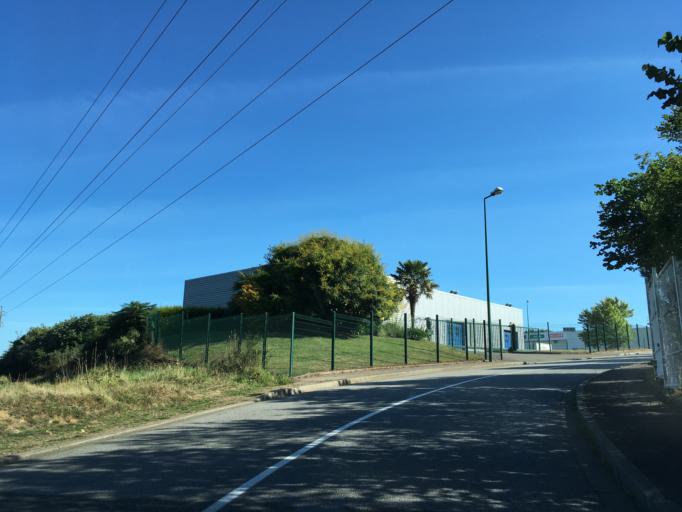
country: FR
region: Brittany
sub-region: Departement du Finistere
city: Quimper
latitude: 48.0103
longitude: -4.0710
